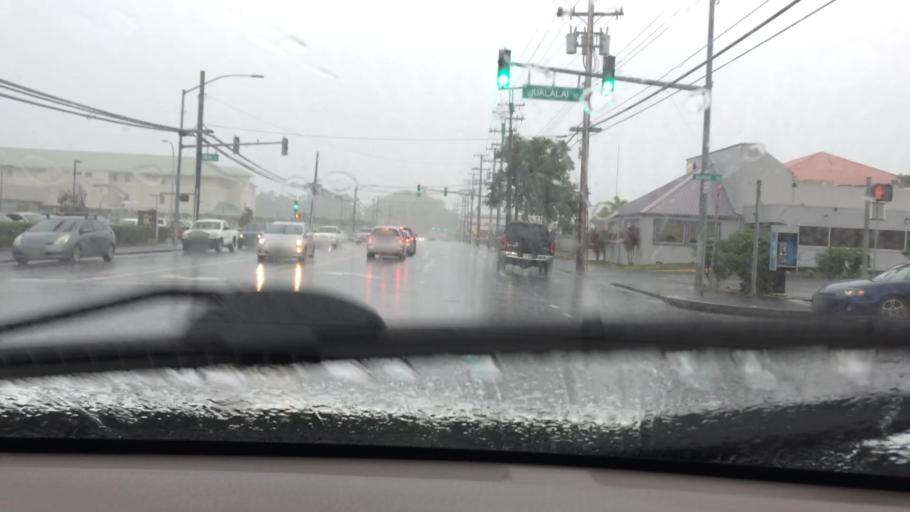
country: US
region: Hawaii
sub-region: Hawaii County
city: Hilo
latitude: 19.7187
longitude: -155.0813
